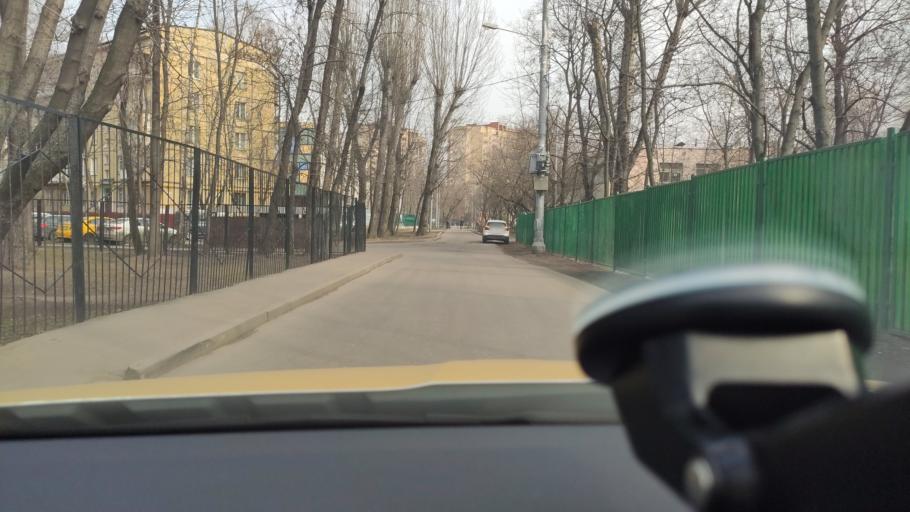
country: RU
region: Moscow
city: Novyye Kuz'minki
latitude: 55.7099
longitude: 37.7546
